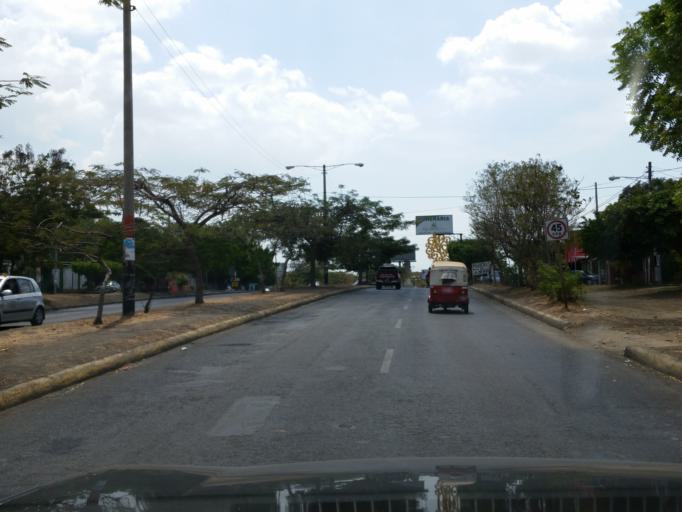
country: NI
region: Managua
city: Managua
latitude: 12.1422
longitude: -86.2222
